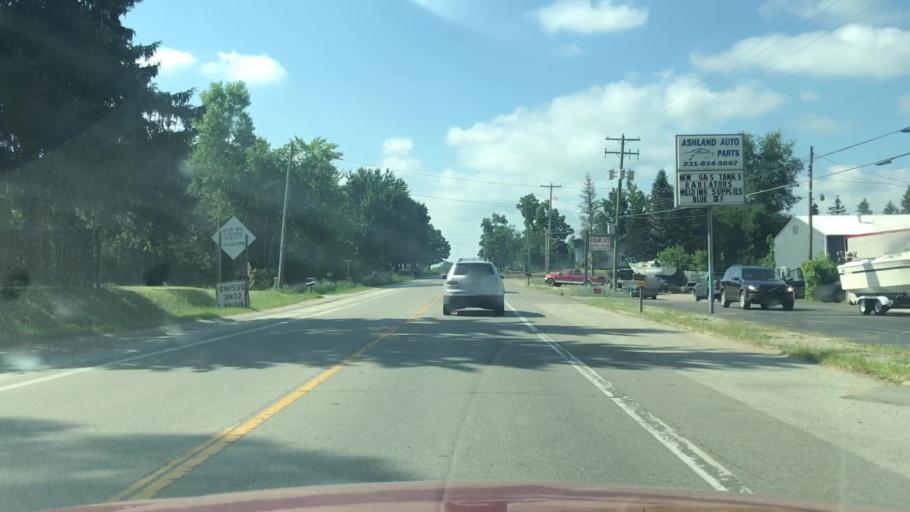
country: US
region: Michigan
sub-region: Newaygo County
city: Newaygo
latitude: 43.3181
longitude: -85.8107
